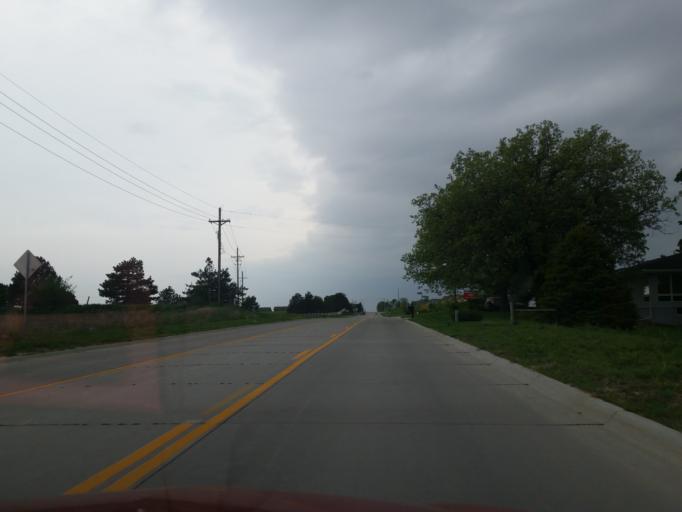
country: US
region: Nebraska
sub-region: Douglas County
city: Bennington
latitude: 41.3212
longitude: -96.1282
